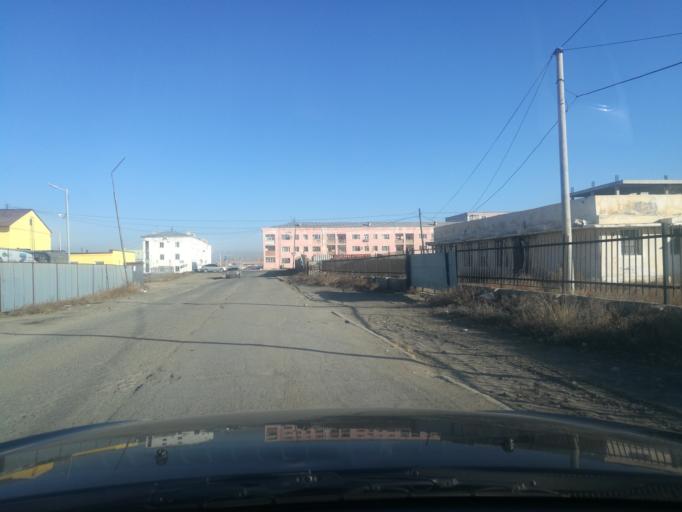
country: MN
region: Ulaanbaatar
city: Ulaanbaatar
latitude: 47.8549
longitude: 106.7575
